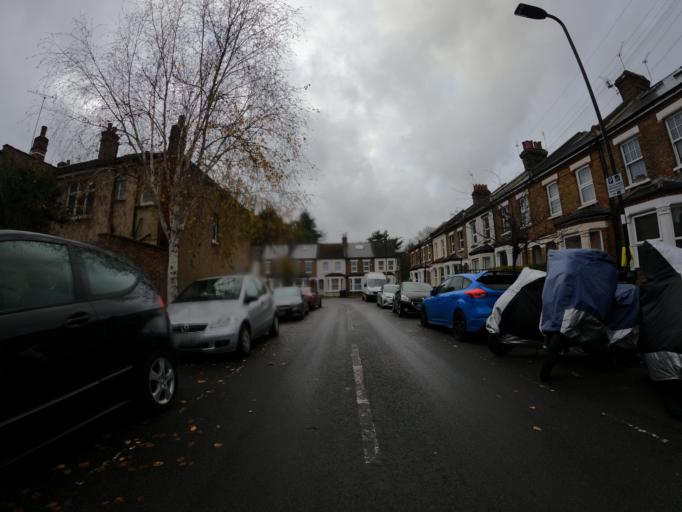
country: GB
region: England
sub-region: Greater London
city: Ealing
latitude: 51.5123
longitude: -0.3287
